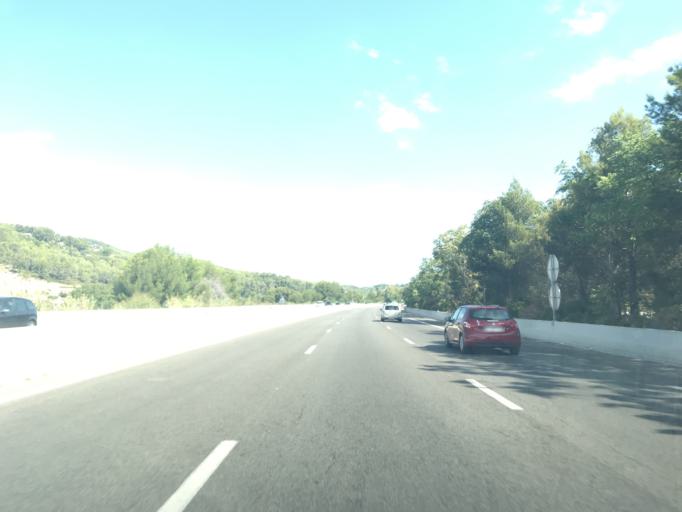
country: FR
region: Provence-Alpes-Cote d'Azur
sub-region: Departement du Var
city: Bandol
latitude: 43.1518
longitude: 5.7652
